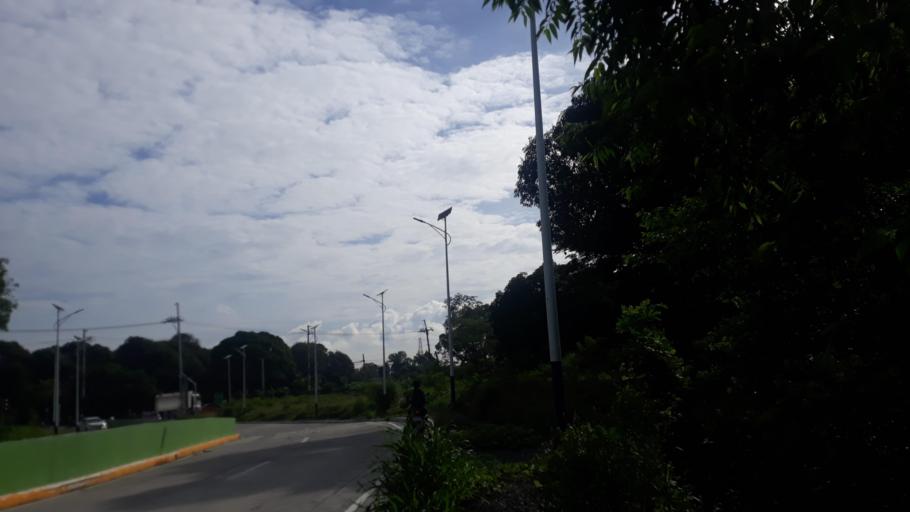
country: PH
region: Calabarzon
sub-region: Province of Cavite
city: Bulihan
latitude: 14.2923
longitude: 120.9703
